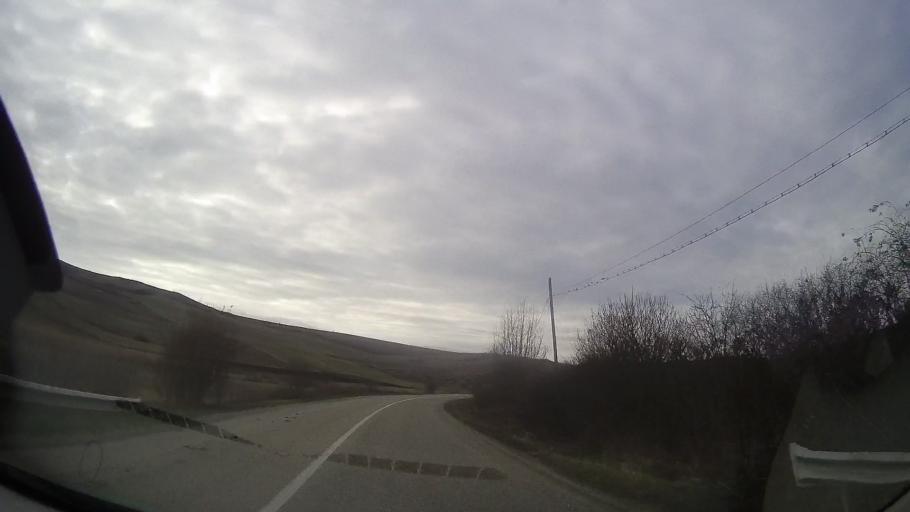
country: RO
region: Bistrita-Nasaud
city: Frunzi
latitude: 46.8939
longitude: 24.3052
